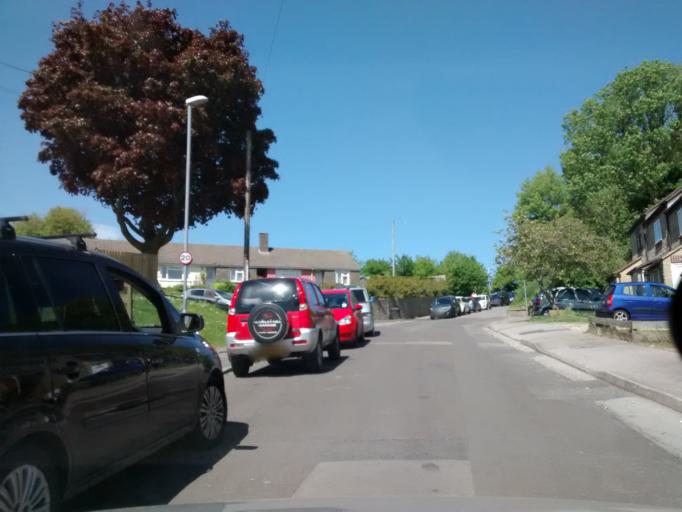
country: GB
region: England
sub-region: Bath and North East Somerset
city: Radstock
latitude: 51.2972
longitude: -2.4420
